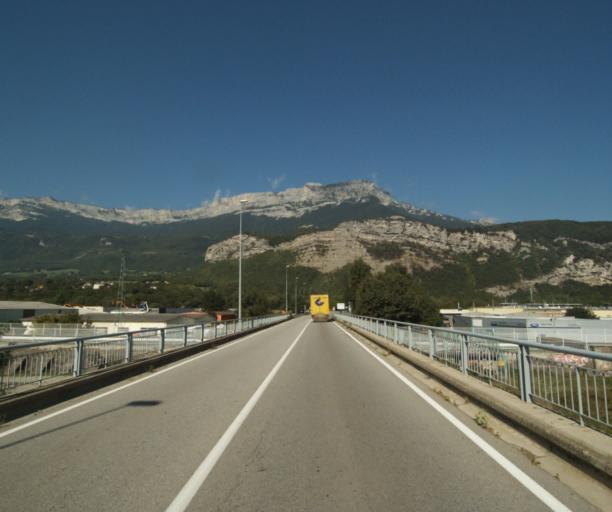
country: FR
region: Rhone-Alpes
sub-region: Departement de l'Isere
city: Le Pont-de-Claix
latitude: 45.1350
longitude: 5.6953
